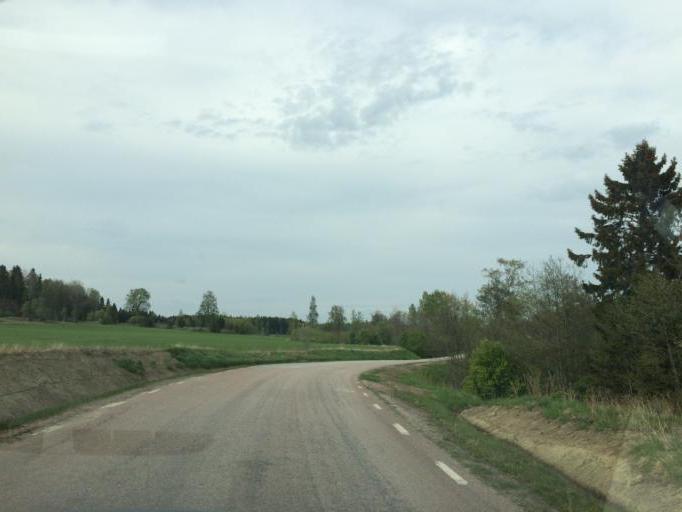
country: SE
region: Vaestmanland
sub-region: Kopings Kommun
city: Koping
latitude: 59.5985
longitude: 16.0038
